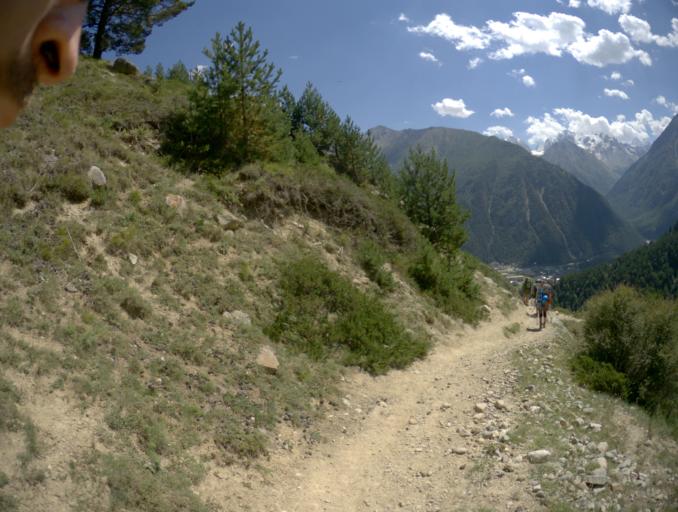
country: RU
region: Kabardino-Balkariya
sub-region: El'brusskiy Rayon
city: El'brus
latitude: 43.2669
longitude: 42.6343
